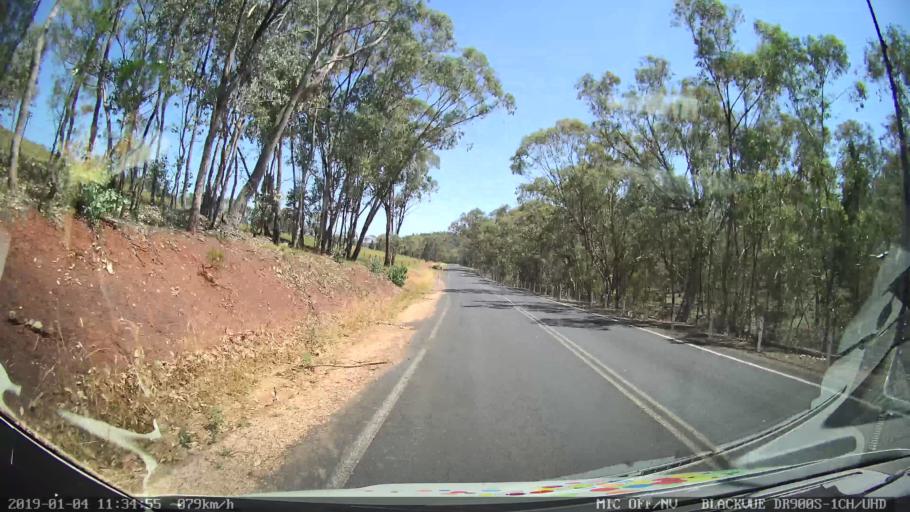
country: AU
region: New South Wales
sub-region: Cabonne
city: Molong
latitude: -33.0615
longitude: 148.8247
